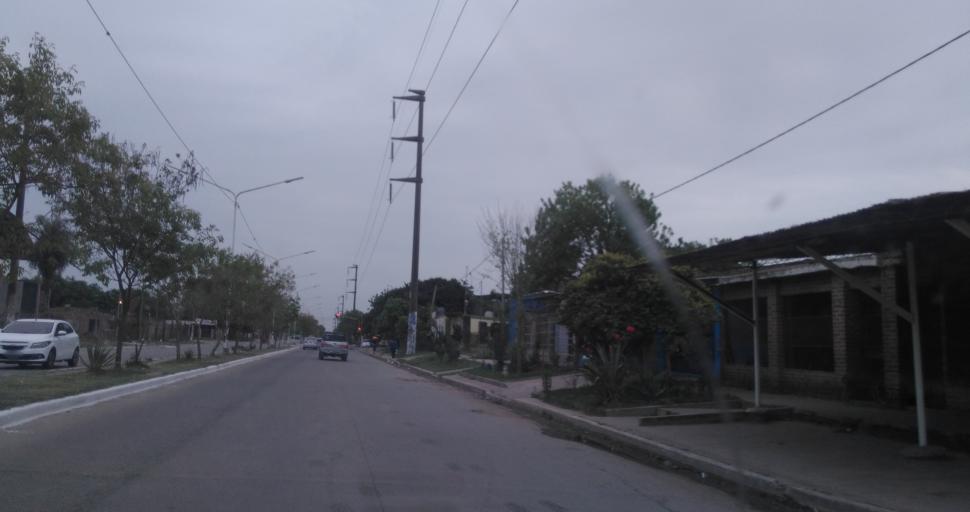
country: AR
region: Chaco
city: Fontana
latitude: -27.4232
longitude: -59.0180
